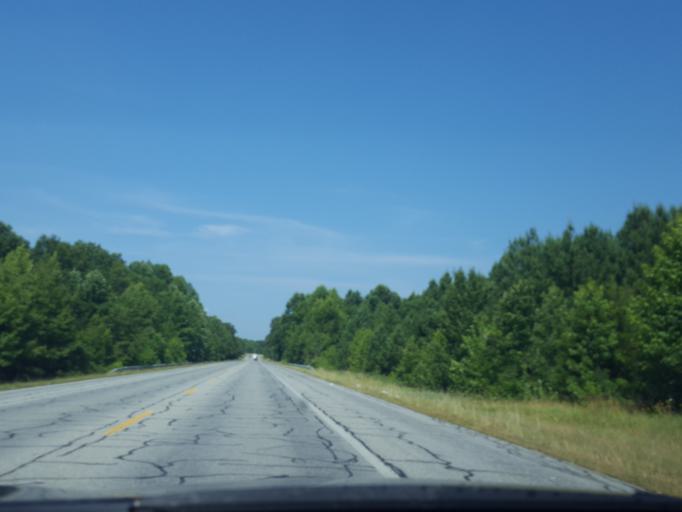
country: US
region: Maryland
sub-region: Saint Mary's County
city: Charlotte Hall
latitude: 38.4740
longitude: -76.8207
